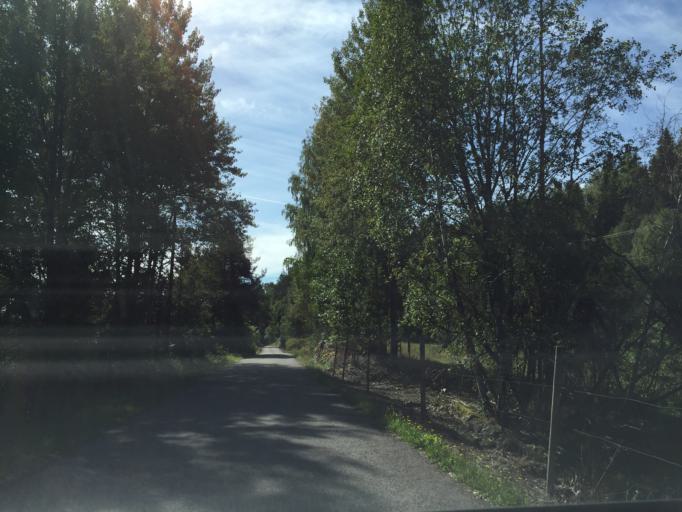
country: NO
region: Vestfold
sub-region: Hof
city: Hof
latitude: 59.4707
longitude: 10.1442
